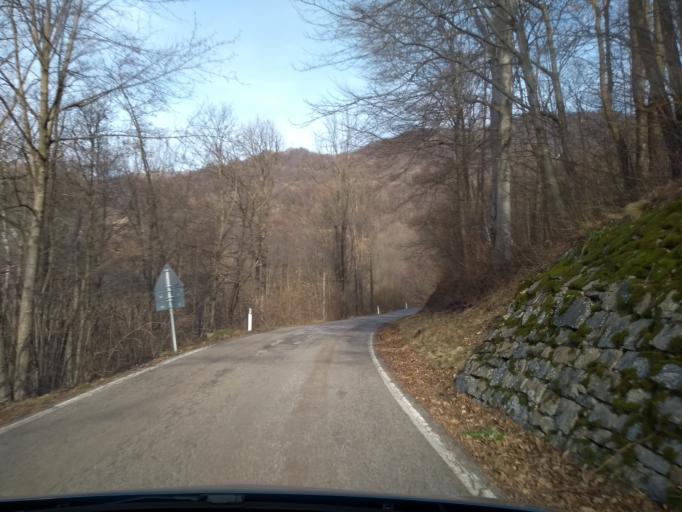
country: IT
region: Piedmont
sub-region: Provincia di Torino
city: Coassolo
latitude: 45.3104
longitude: 7.4791
